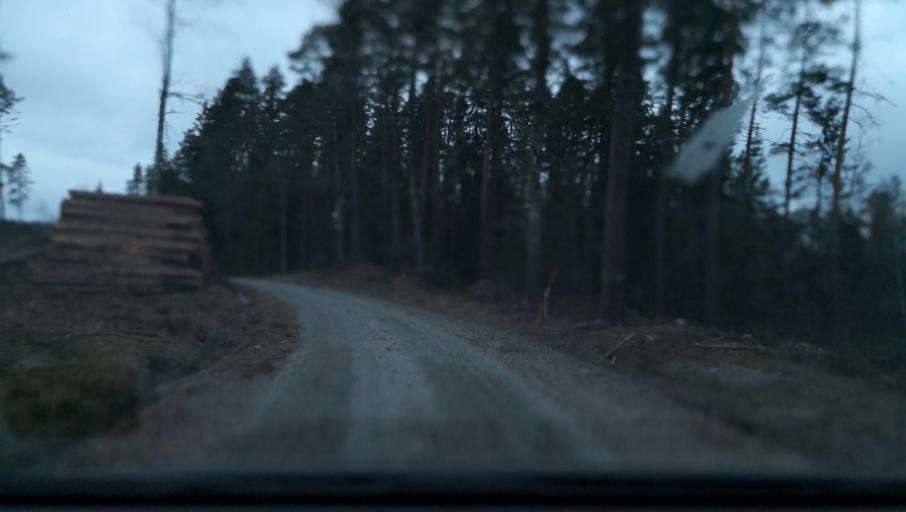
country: SE
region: OErebro
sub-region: Lindesbergs Kommun
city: Fellingsbro
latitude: 59.6147
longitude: 15.5959
